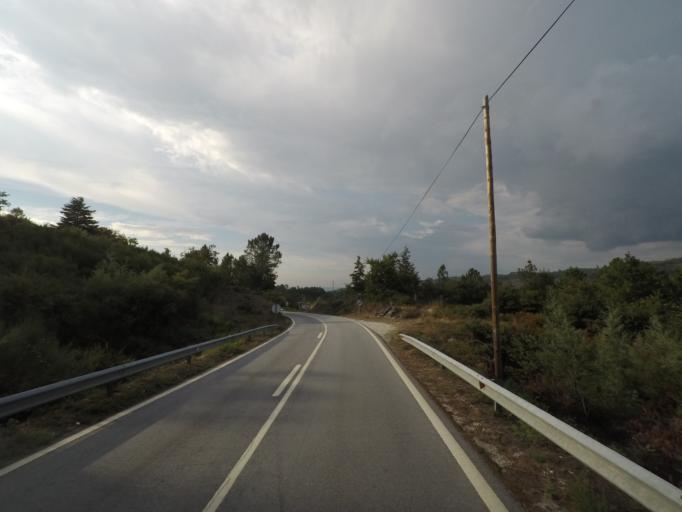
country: PT
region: Porto
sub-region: Baiao
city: Valadares
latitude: 41.2076
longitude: -7.9741
